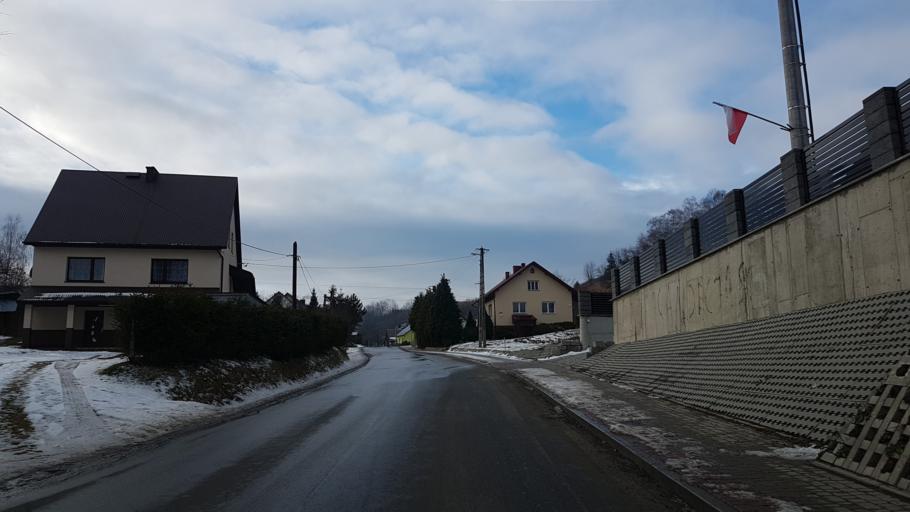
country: PL
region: Lesser Poland Voivodeship
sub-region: Powiat nowosadecki
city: Stary Sacz
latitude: 49.5118
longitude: 20.6056
